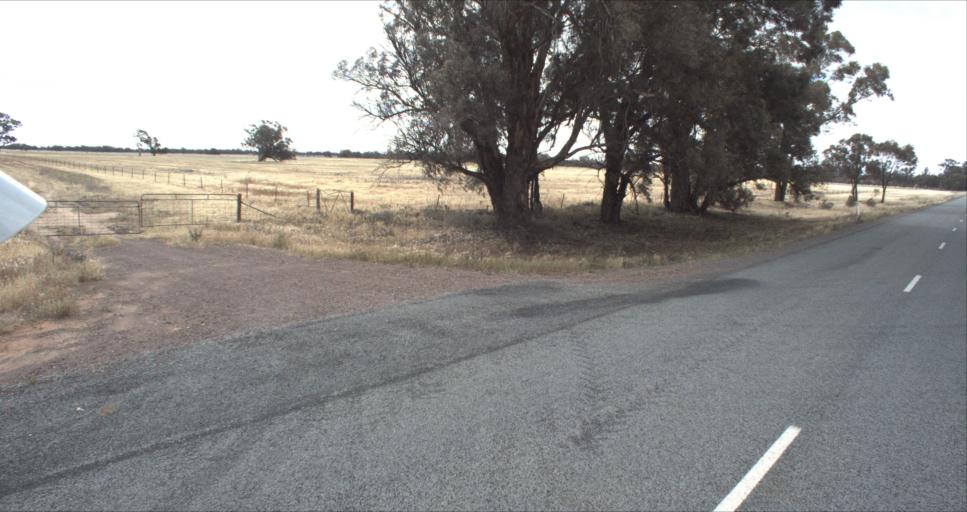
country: AU
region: New South Wales
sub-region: Leeton
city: Leeton
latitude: -34.6720
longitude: 146.3473
